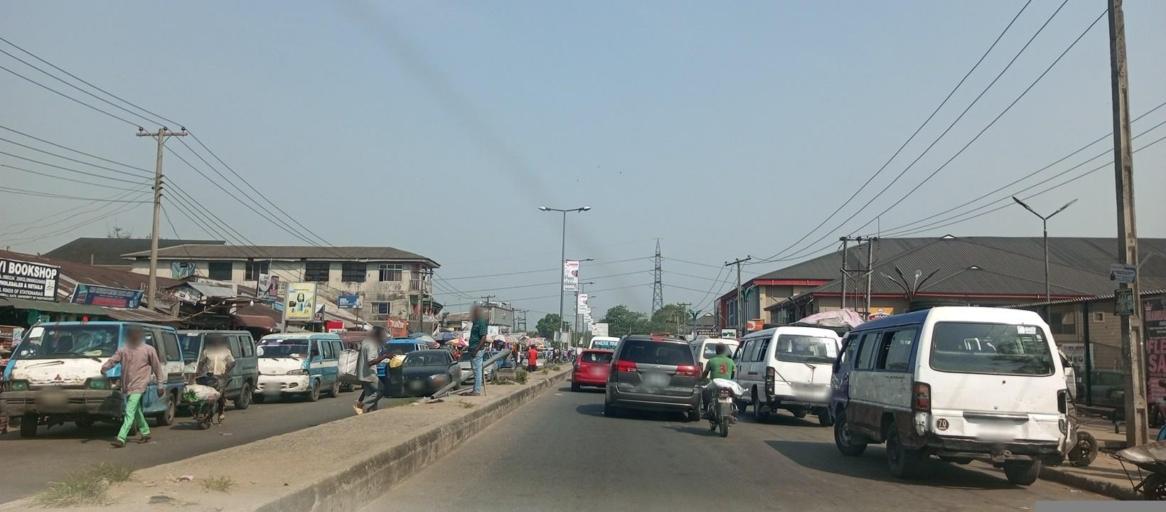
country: NG
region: Rivers
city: Emuoha
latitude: 4.8969
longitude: 6.9076
